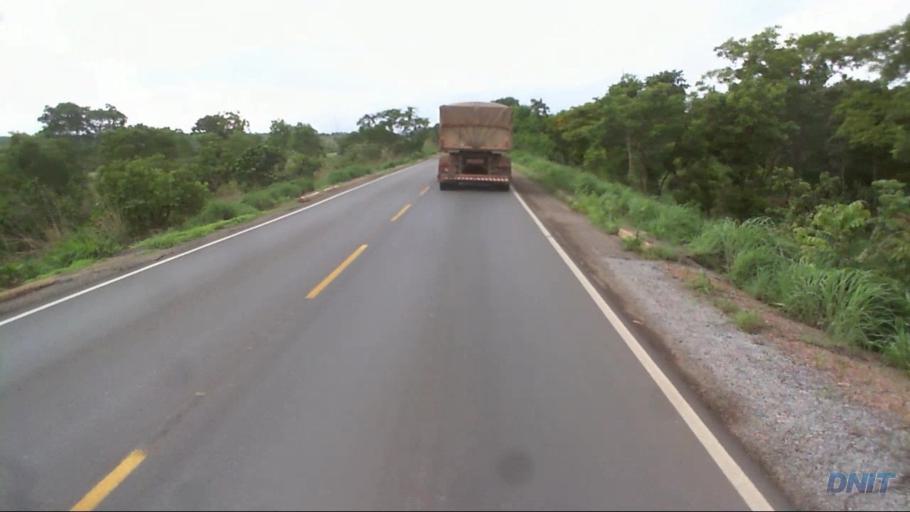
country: BR
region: Goias
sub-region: Padre Bernardo
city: Padre Bernardo
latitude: -15.1877
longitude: -48.2844
